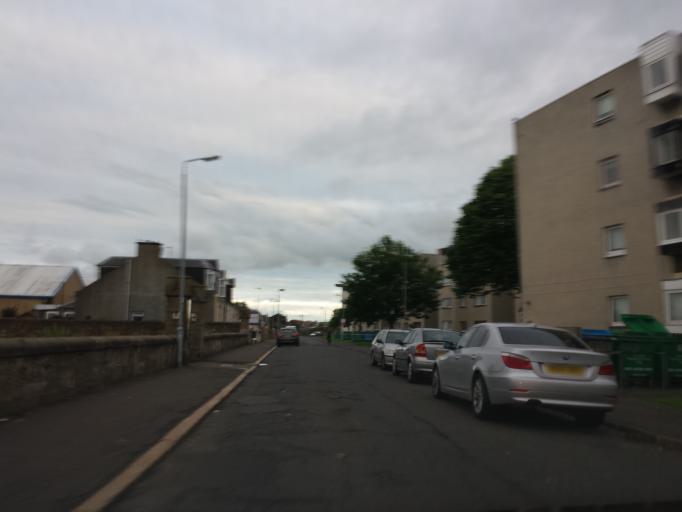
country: GB
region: Scotland
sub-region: South Ayrshire
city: Ayr
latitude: 55.4704
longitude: -4.6259
